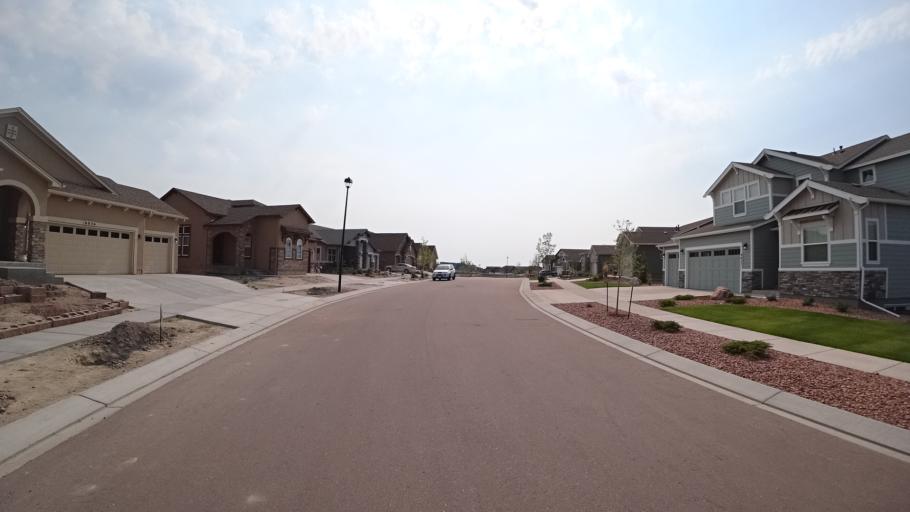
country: US
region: Colorado
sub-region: El Paso County
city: Black Forest
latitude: 38.9735
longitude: -104.7232
